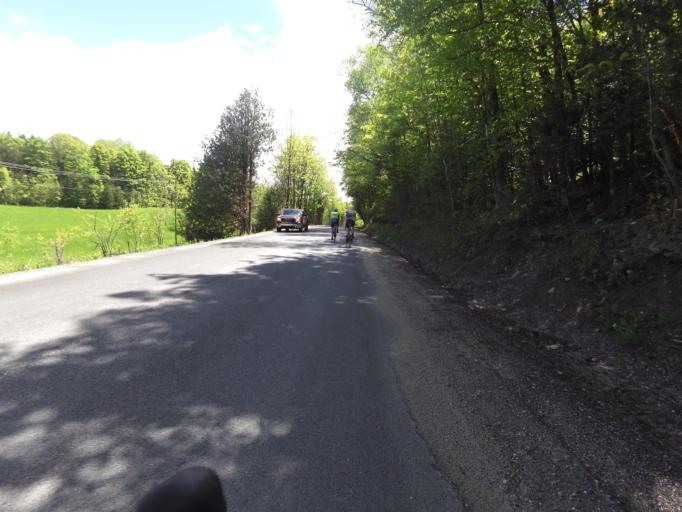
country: CA
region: Quebec
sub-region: Outaouais
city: Wakefield
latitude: 45.6779
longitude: -75.9603
